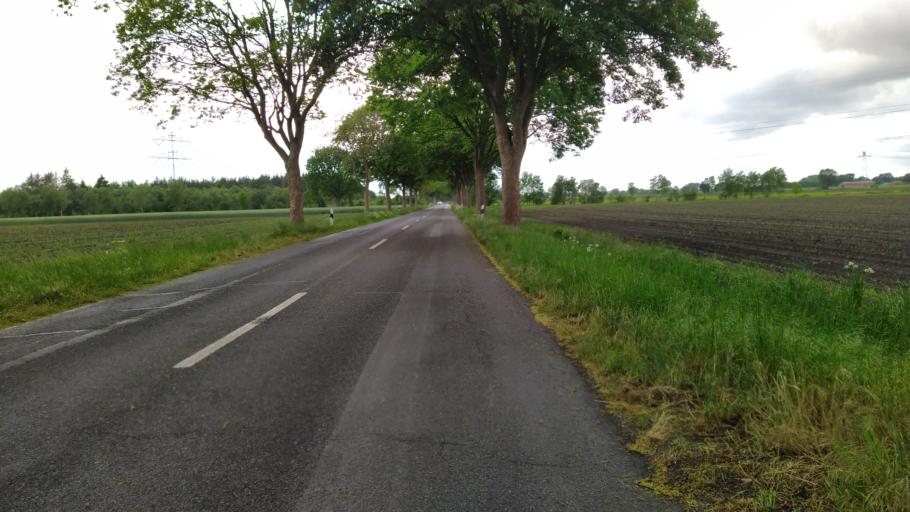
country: DE
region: Lower Saxony
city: Brest
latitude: 53.4538
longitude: 9.4109
